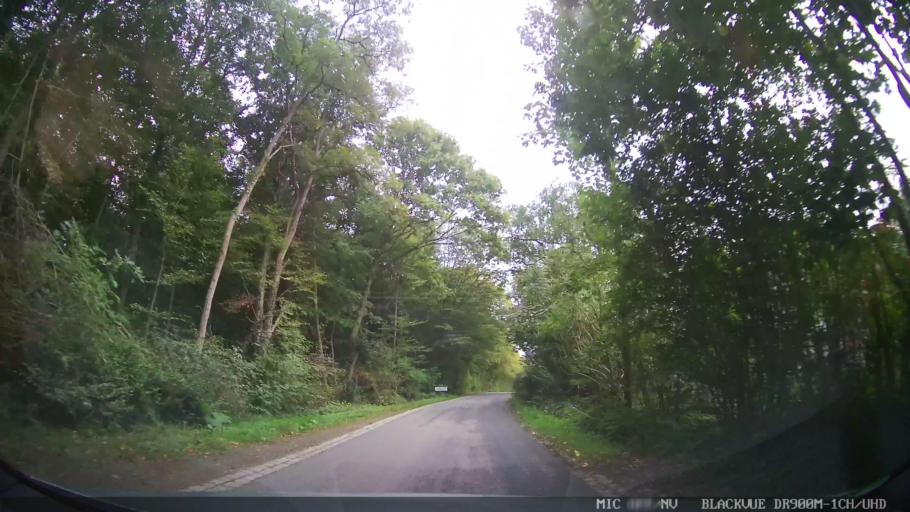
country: DE
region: Schleswig-Holstein
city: Gromitz
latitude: 54.1852
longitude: 10.9669
